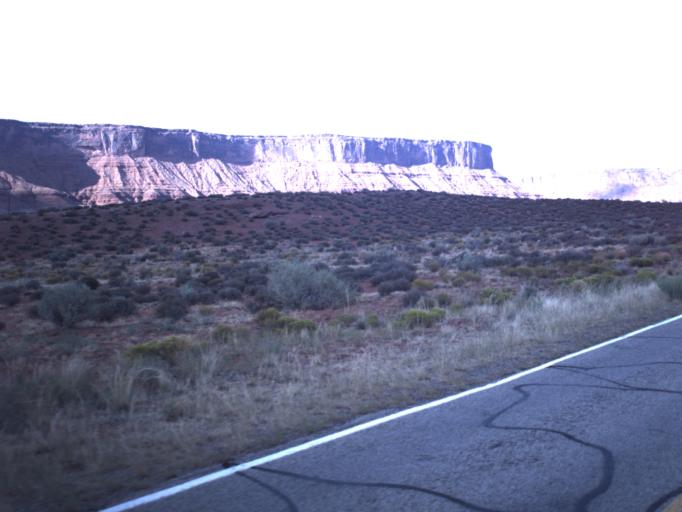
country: US
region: Utah
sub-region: Grand County
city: Moab
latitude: 38.7233
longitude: -109.3571
